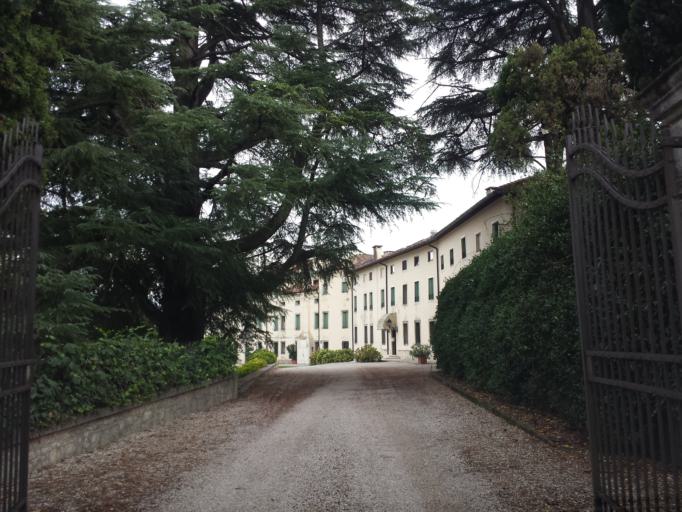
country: IT
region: Veneto
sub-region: Provincia di Vicenza
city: Arcugnano-Torri
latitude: 45.4972
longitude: 11.5392
